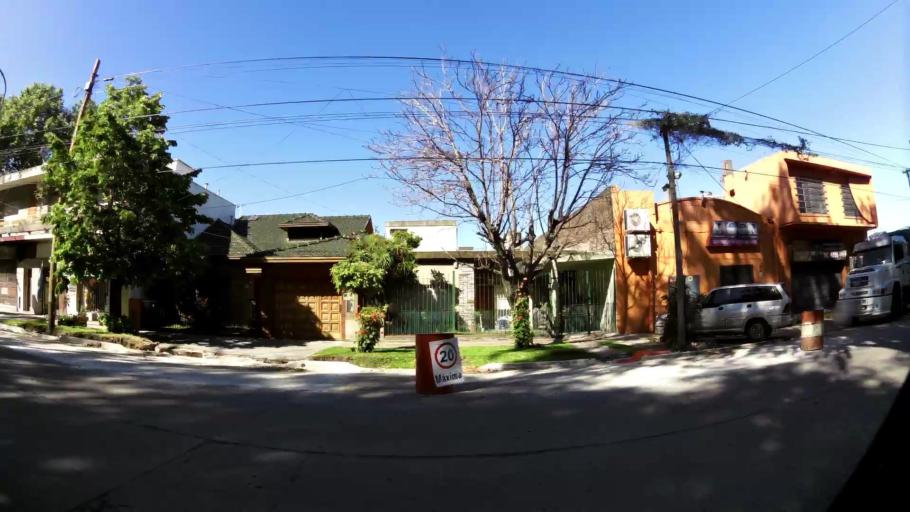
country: AR
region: Buenos Aires
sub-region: Partido de Quilmes
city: Quilmes
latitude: -34.7052
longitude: -58.2905
